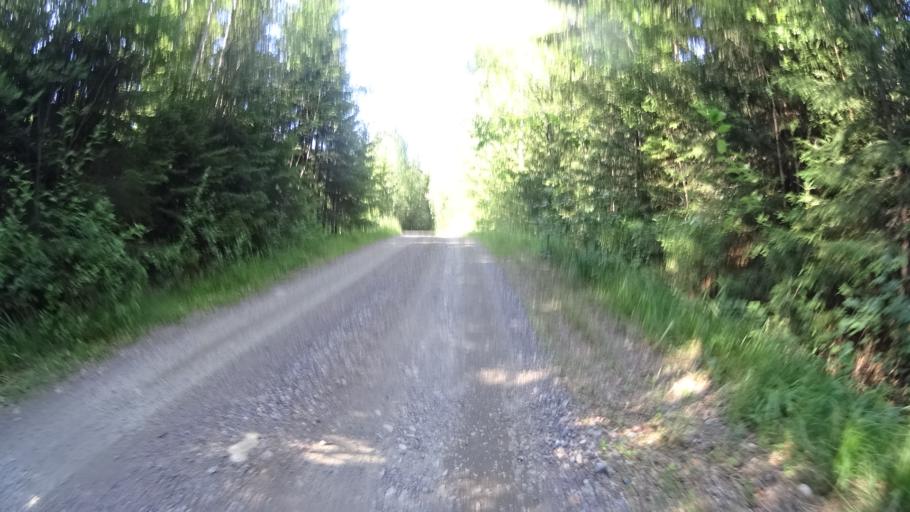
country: FI
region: Uusimaa
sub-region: Helsinki
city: Karkkila
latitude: 60.6469
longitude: 24.1655
